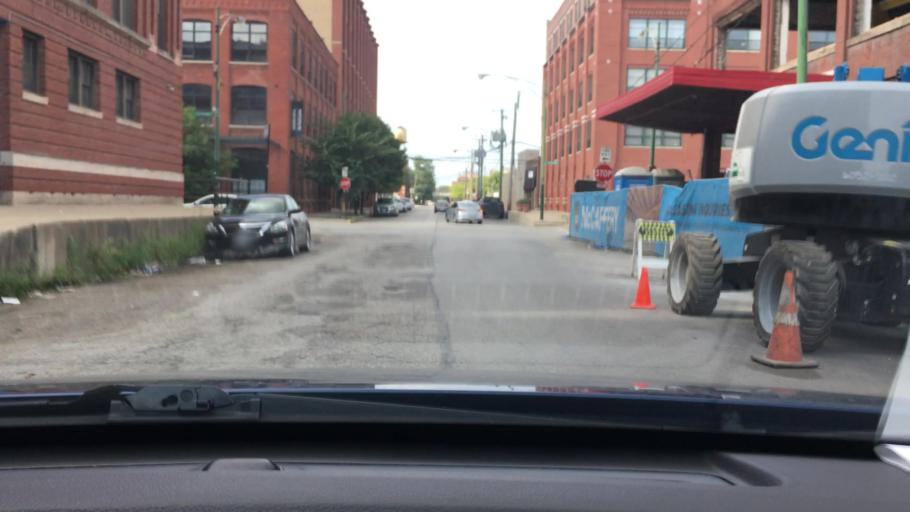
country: US
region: Illinois
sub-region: Cook County
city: Chicago
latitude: 41.8863
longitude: -87.6556
